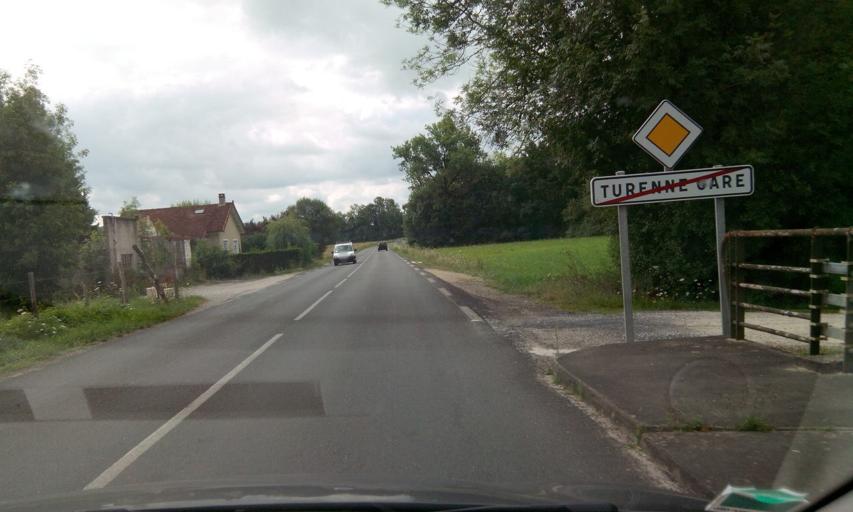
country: FR
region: Limousin
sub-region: Departement de la Correze
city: Meyssac
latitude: 45.0352
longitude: 1.6035
